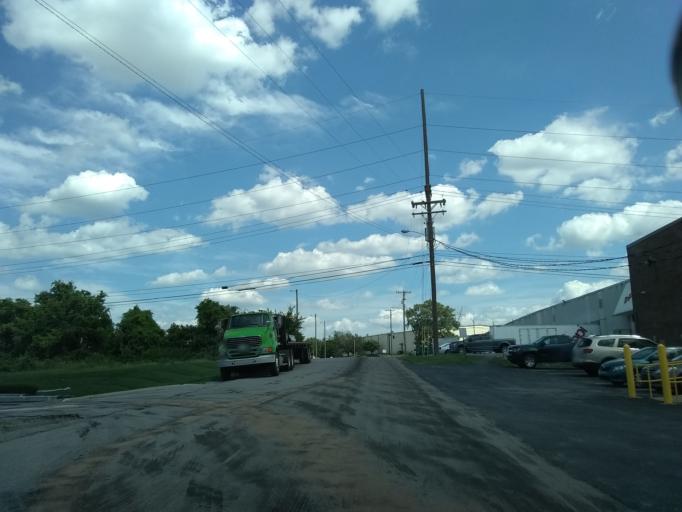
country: US
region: Tennessee
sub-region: Davidson County
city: Nashville
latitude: 36.1504
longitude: -86.7087
